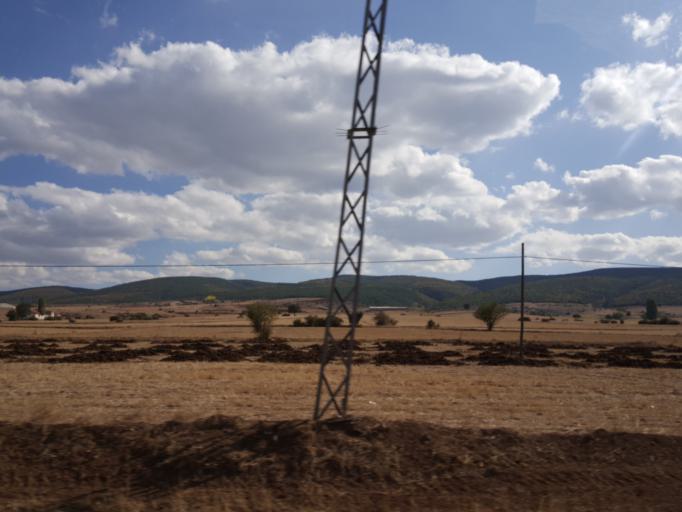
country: TR
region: Tokat
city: Yesilyurt
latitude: 40.0092
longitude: 36.1895
